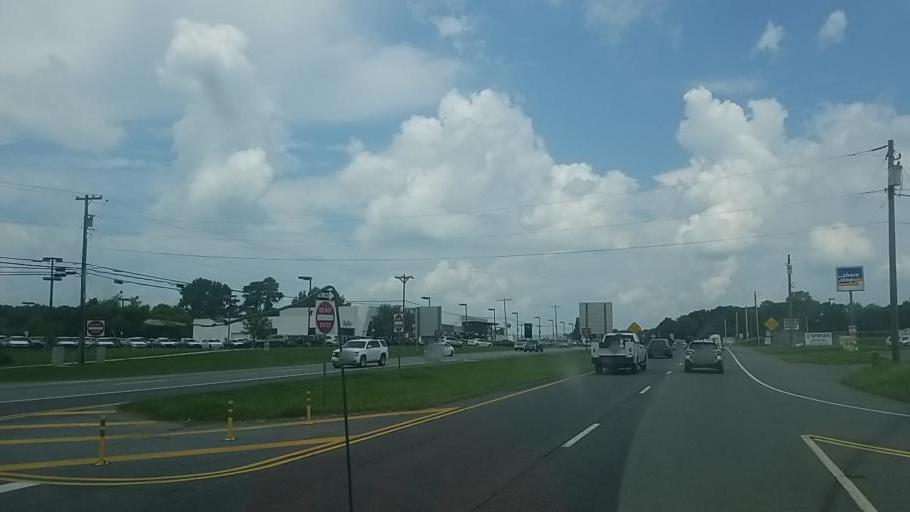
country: US
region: Delaware
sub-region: Sussex County
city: Milford
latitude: 38.9448
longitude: -75.4265
